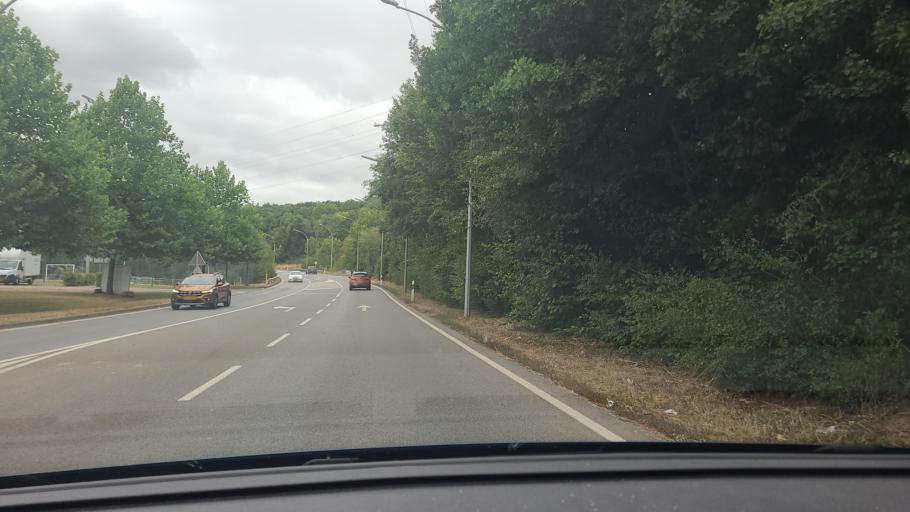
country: LU
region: Luxembourg
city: Lamadelaine
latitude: 49.5566
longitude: 5.8590
